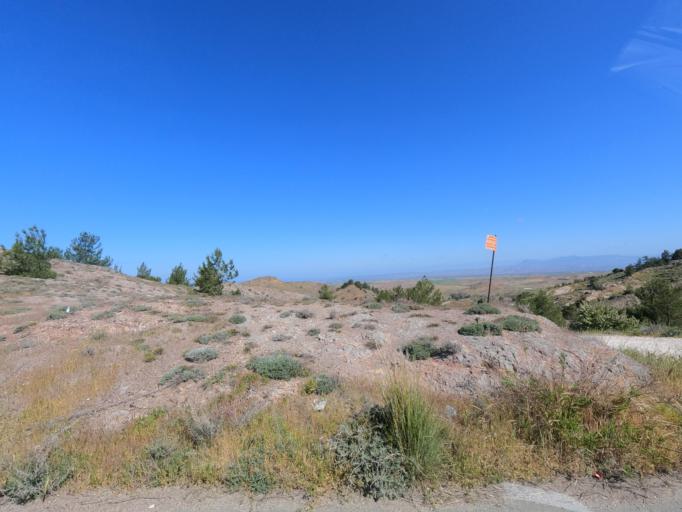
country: CY
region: Lefkosia
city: Peristerona
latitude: 35.0584
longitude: 33.0578
